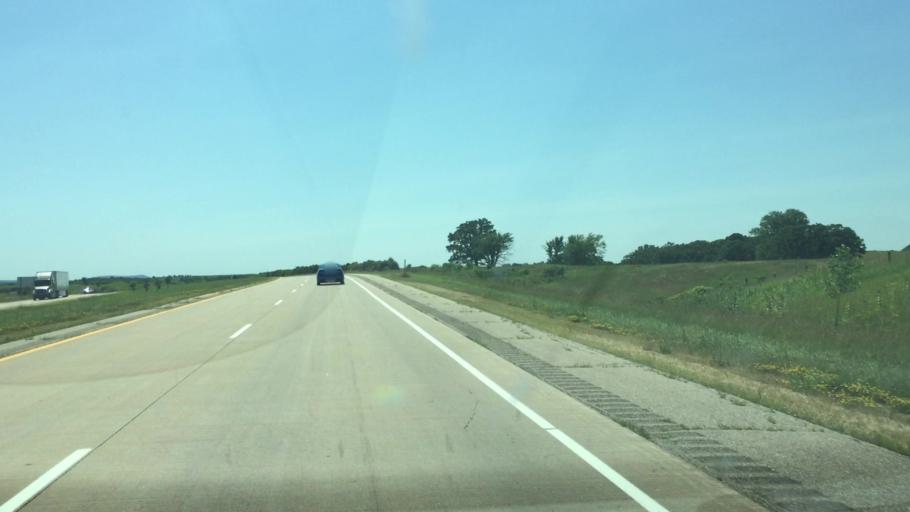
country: US
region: Wisconsin
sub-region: Iowa County
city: Mineral Point
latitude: 42.8808
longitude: -90.1835
